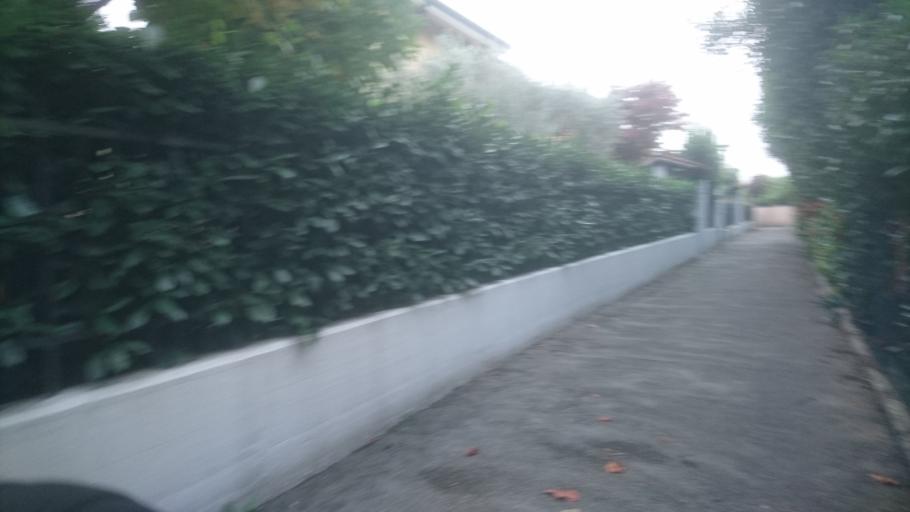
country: IT
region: Veneto
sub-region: Provincia di Padova
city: Tencarola
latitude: 45.3968
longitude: 11.8139
